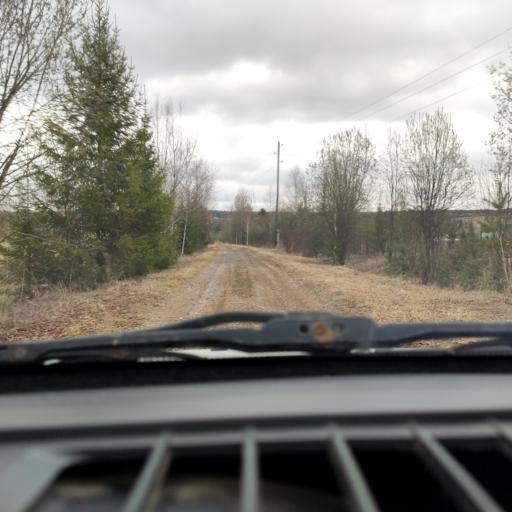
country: RU
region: Perm
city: Kultayevo
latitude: 57.8271
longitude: 55.7772
